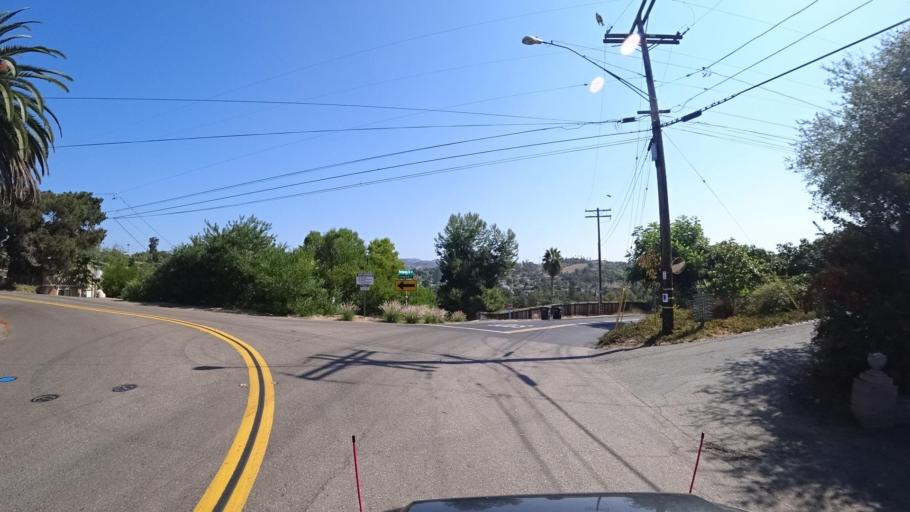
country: US
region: California
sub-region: San Diego County
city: Vista
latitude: 33.1841
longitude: -117.2172
